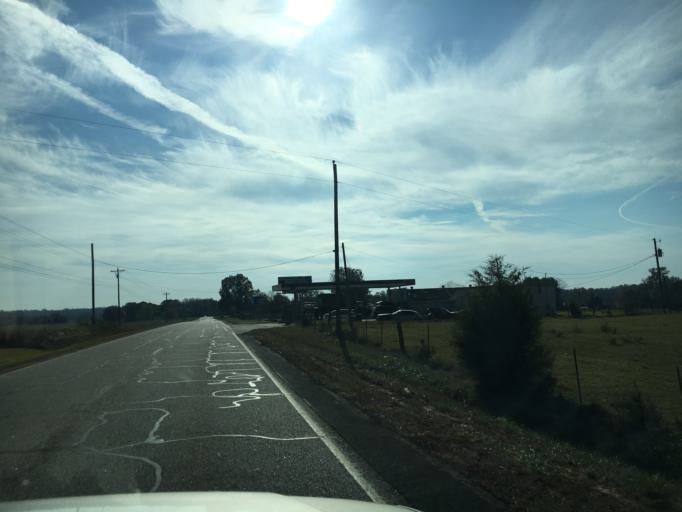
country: US
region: Georgia
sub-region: Hart County
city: Hartwell
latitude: 34.2588
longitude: -82.8979
